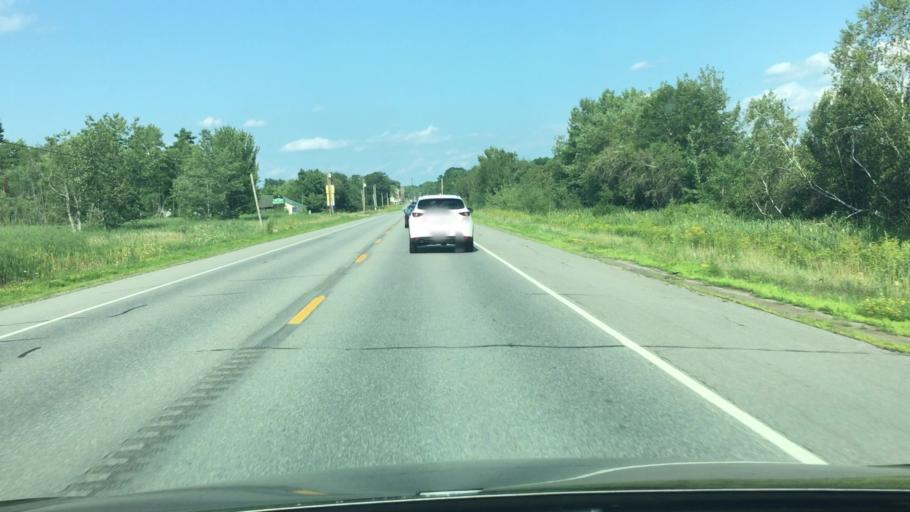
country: US
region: Maine
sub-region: Kennebec County
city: Windsor
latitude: 44.3897
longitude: -69.5866
